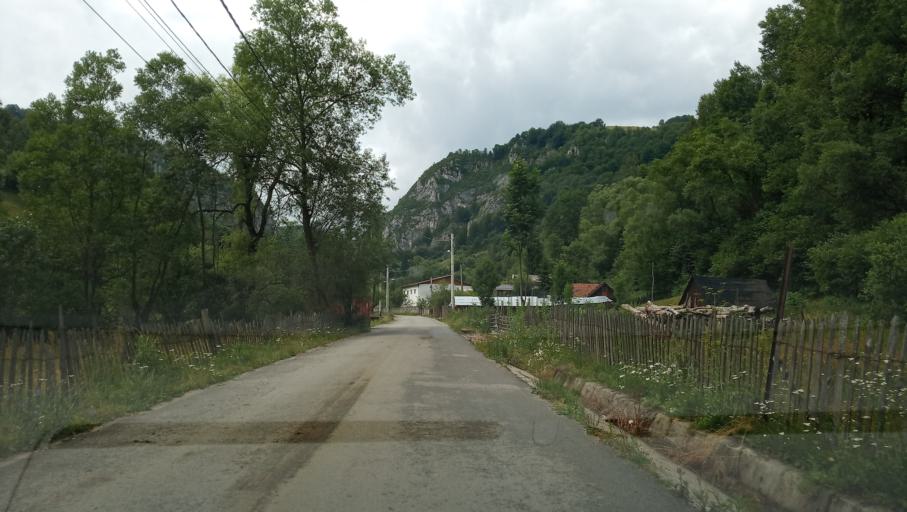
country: RO
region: Hunedoara
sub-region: Oras Petrila
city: Petrila
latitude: 45.4640
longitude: 23.4202
